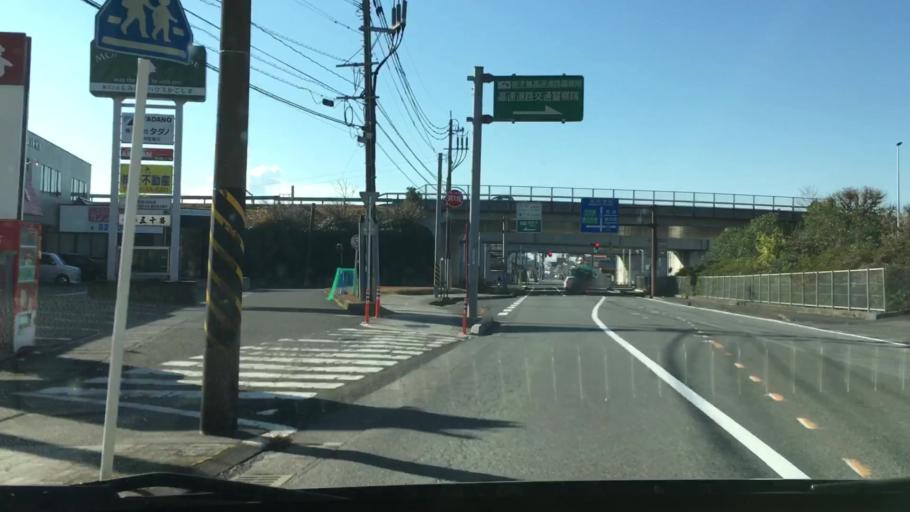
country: JP
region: Kagoshima
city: Kajiki
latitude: 31.7469
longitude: 130.6706
